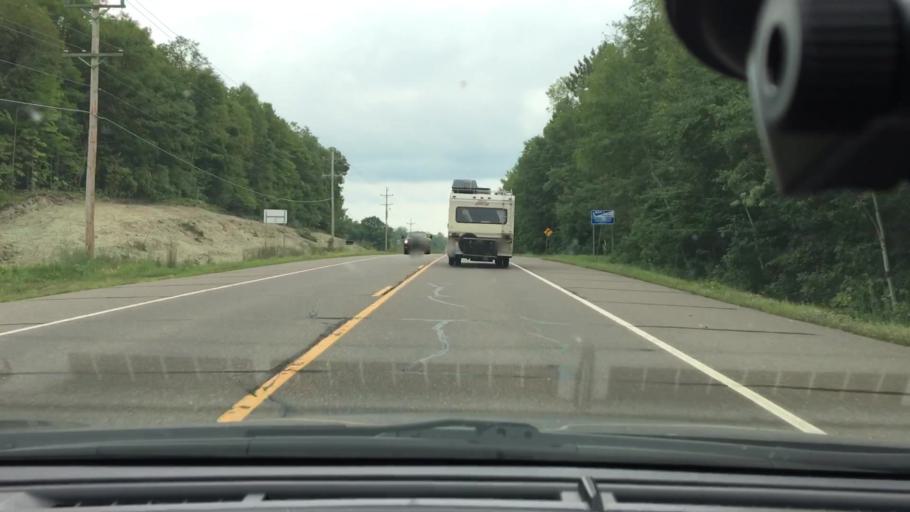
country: US
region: Minnesota
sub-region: Crow Wing County
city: Crosby
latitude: 46.4874
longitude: -93.9034
